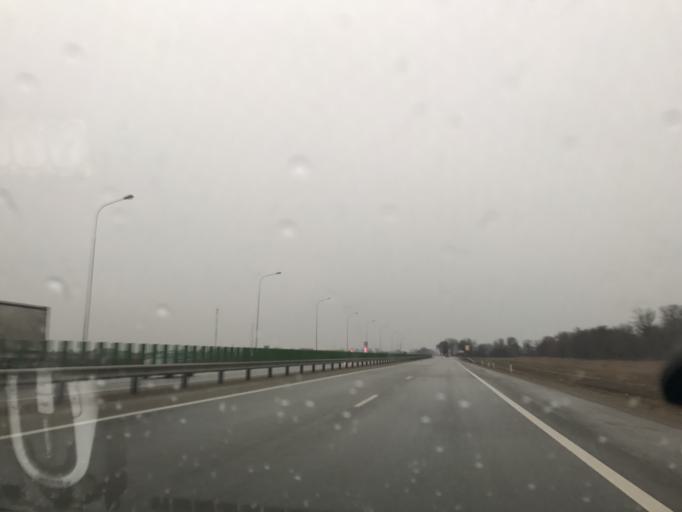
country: RU
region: Krasnodarskiy
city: Pavlovskaya
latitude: 46.2737
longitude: 39.8316
